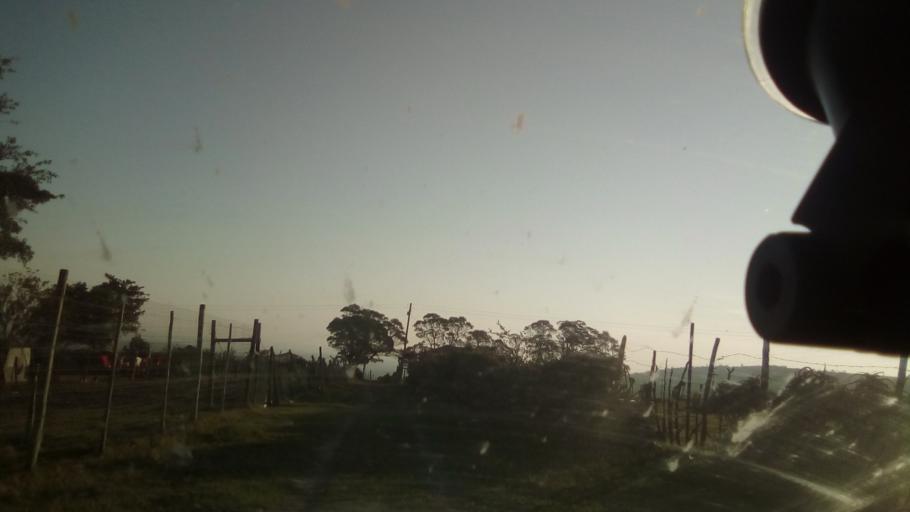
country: ZA
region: Eastern Cape
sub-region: Buffalo City Metropolitan Municipality
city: Bhisho
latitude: -32.9727
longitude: 27.2942
